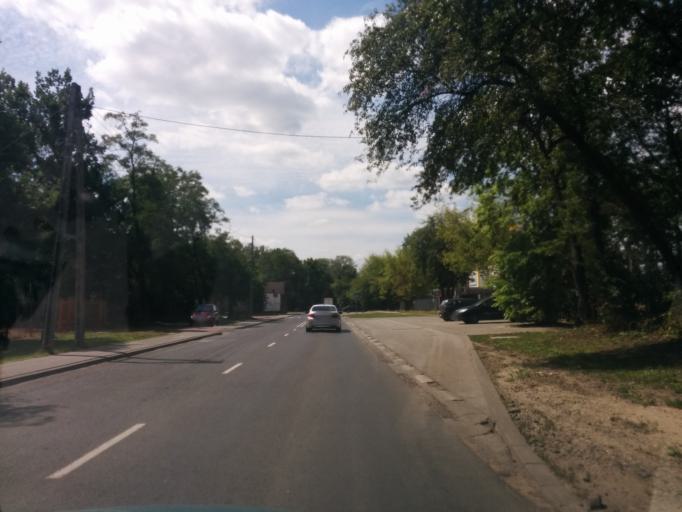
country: PL
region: Masovian Voivodeship
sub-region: Warszawa
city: Bialoleka
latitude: 52.3338
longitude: 20.9699
